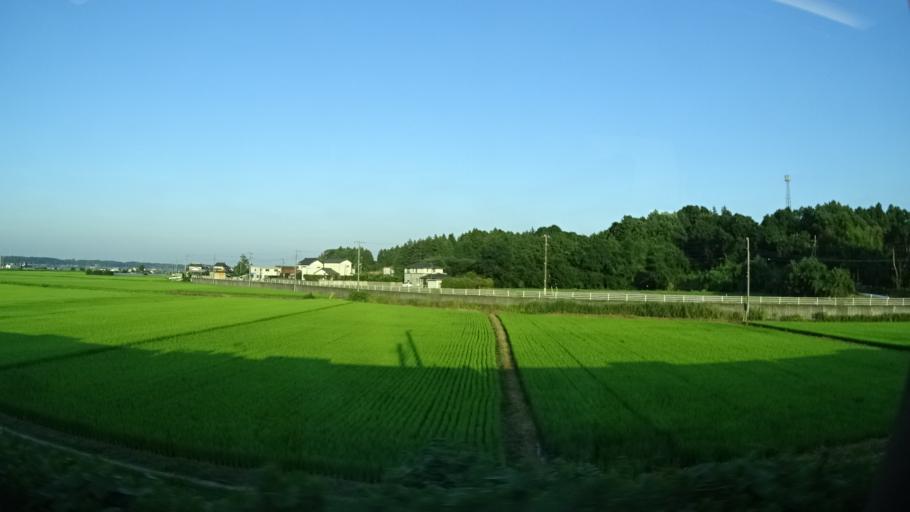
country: JP
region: Ibaraki
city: Ishioka
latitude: 36.1543
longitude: 140.2889
